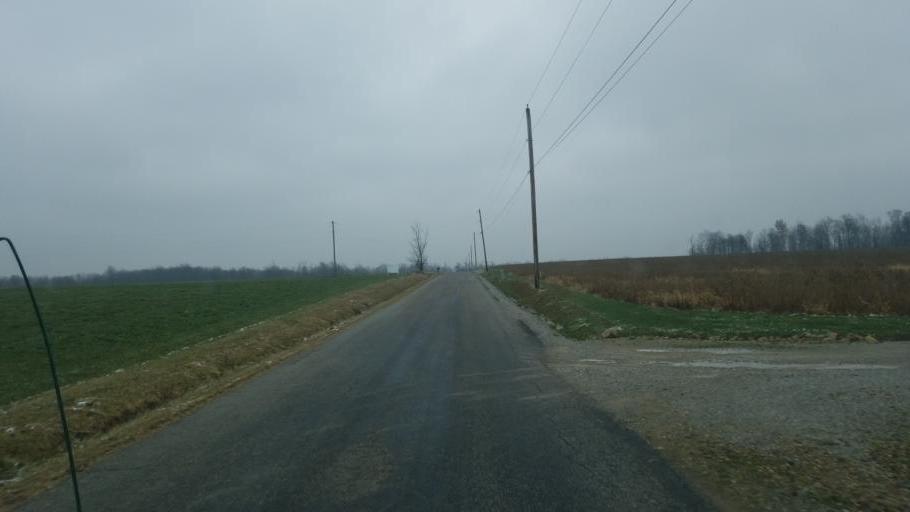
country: US
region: Ohio
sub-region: Huron County
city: New London
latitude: 41.0160
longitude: -82.3403
